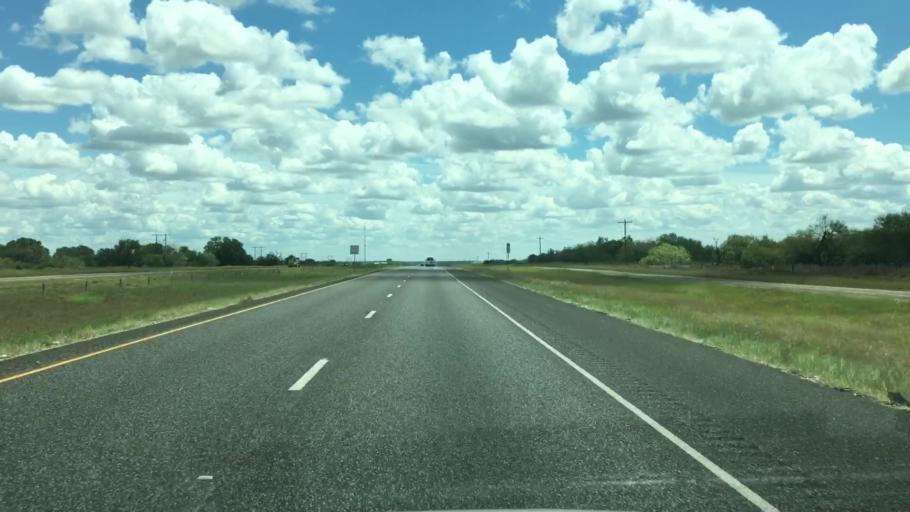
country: US
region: Texas
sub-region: Atascosa County
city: Pleasanton
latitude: 28.8173
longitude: -98.3585
